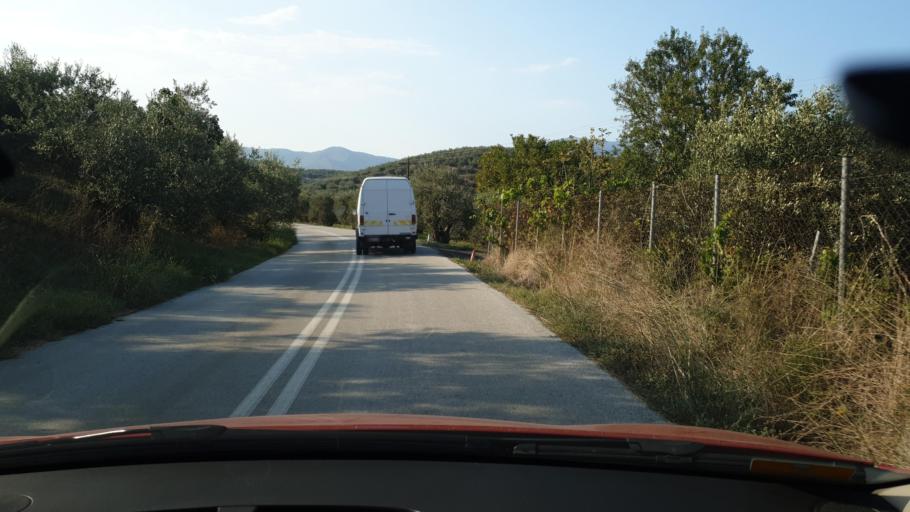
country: GR
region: Thessaly
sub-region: Nomos Magnisias
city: Pteleos
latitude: 38.9902
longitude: 22.9646
